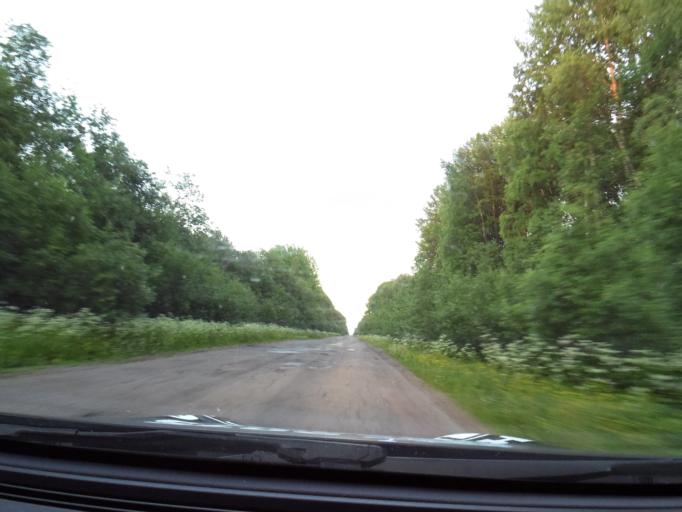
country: RU
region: Leningrad
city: Voznesen'ye
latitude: 60.8463
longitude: 35.6063
